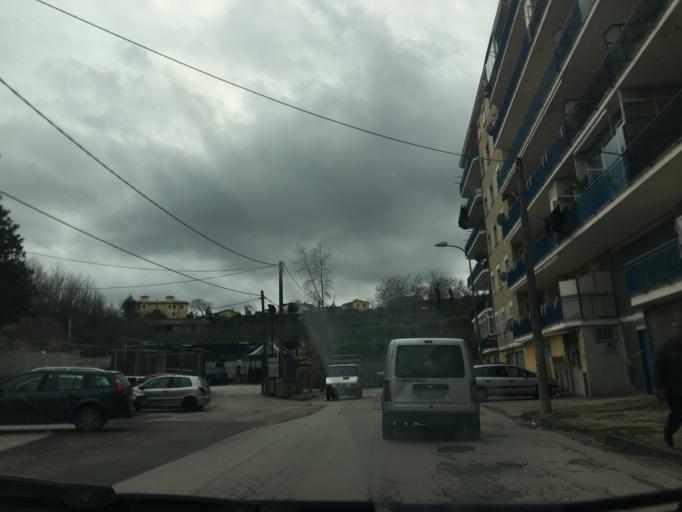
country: IT
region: Campania
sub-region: Provincia di Napoli
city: Mugnano di Napoli
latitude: 40.8951
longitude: 14.2026
